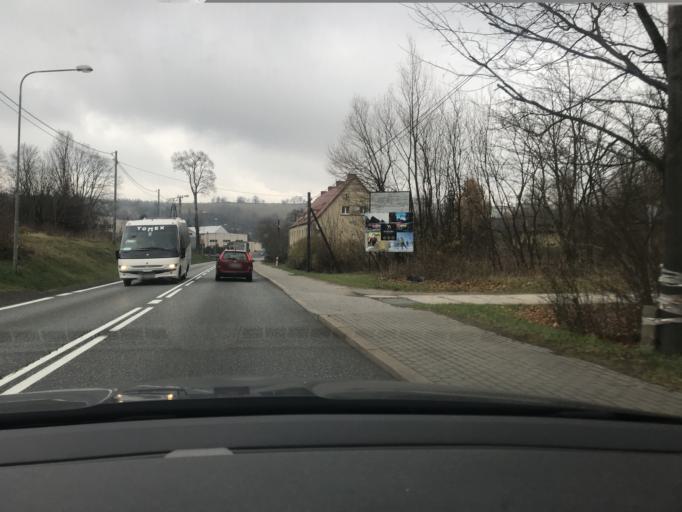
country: PL
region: Lower Silesian Voivodeship
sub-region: Powiat klodzki
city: Duszniki-Zdroj
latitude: 50.4027
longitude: 16.3824
